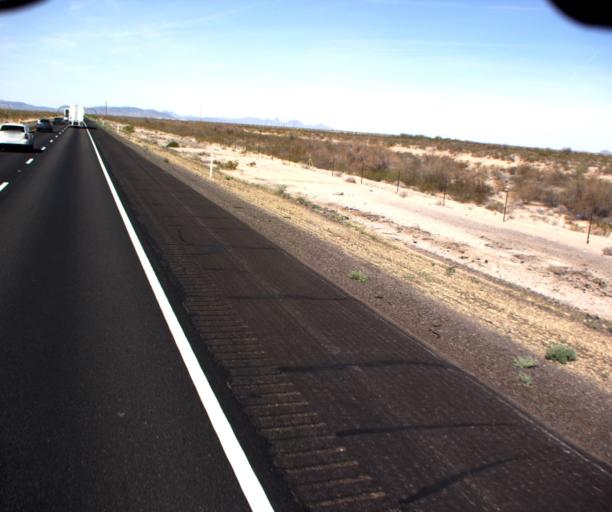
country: US
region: Arizona
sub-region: La Paz County
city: Salome
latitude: 33.6203
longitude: -113.6930
